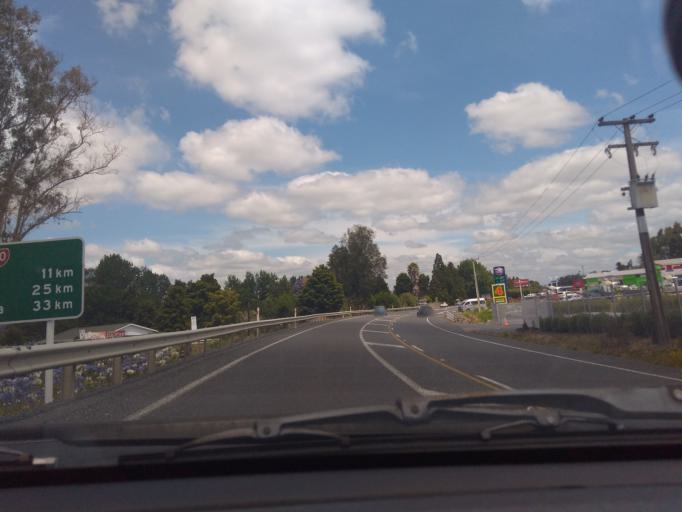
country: NZ
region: Northland
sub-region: Far North District
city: Kerikeri
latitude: -35.2086
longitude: 173.9200
